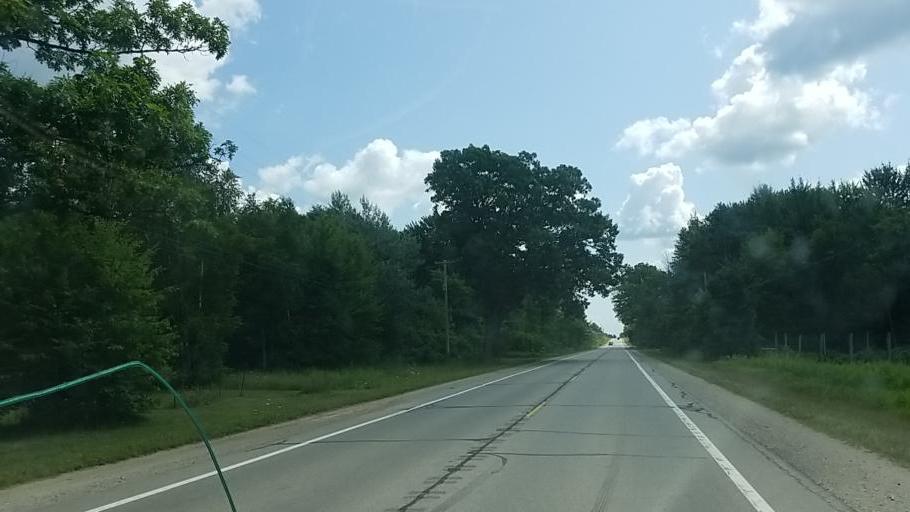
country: US
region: Michigan
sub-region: Muskegon County
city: Ravenna
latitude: 43.2352
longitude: -85.9588
